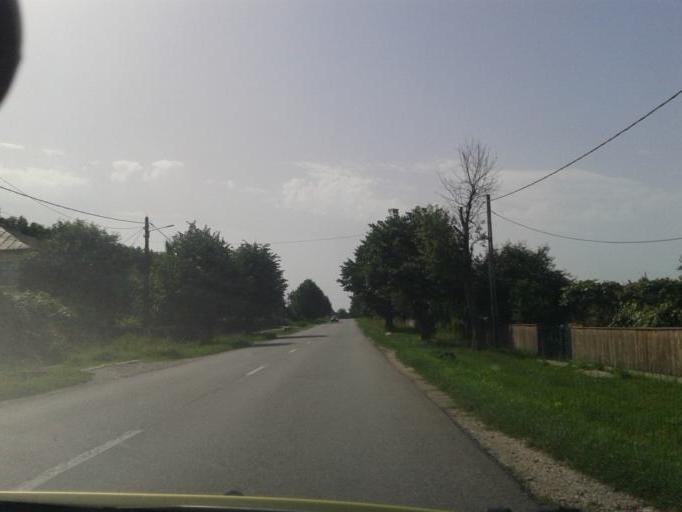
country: RO
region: Valcea
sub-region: Oras Baile Govora
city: Baile Govora
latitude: 45.0943
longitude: 24.2133
